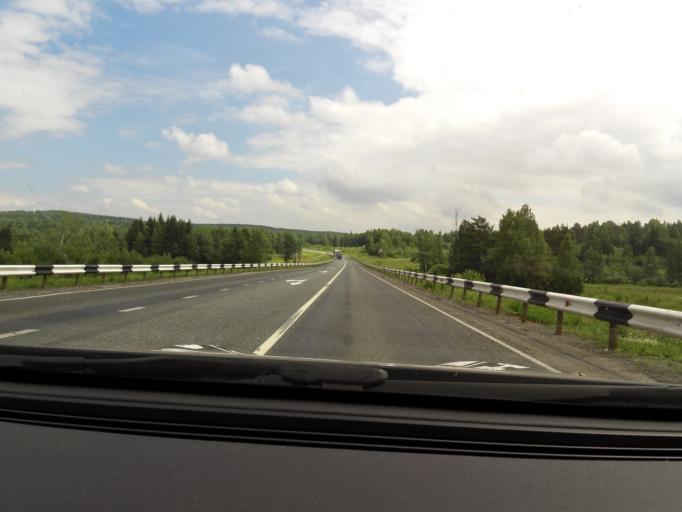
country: RU
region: Perm
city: Suksun
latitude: 57.0940
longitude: 57.3563
